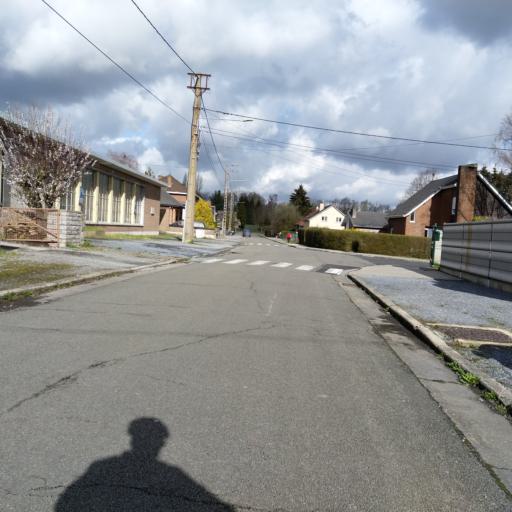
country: BE
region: Wallonia
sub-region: Province du Hainaut
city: Mons
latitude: 50.4819
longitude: 3.9420
